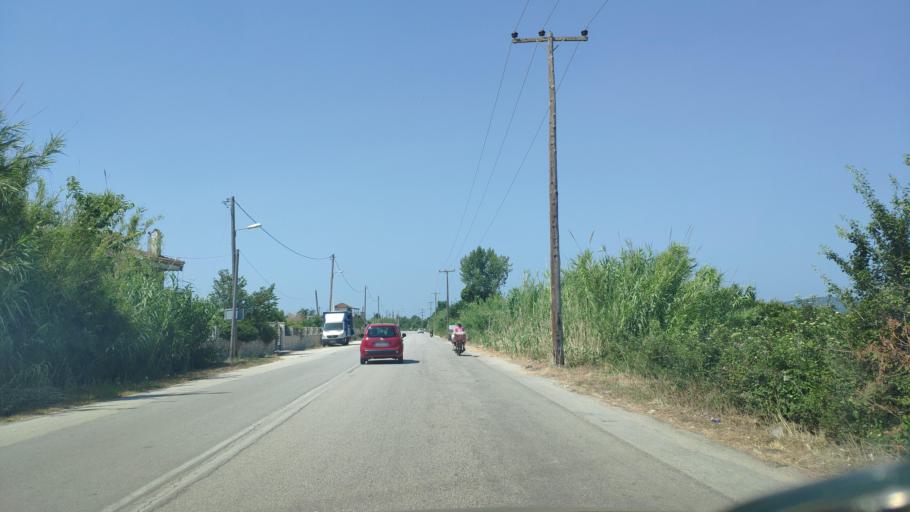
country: GR
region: Epirus
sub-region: Nomos Artas
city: Kostakioi
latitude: 39.1272
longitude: 20.9448
